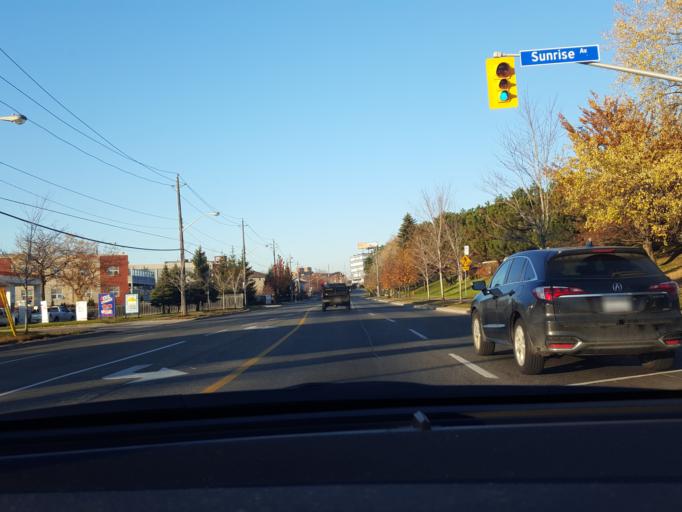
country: CA
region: Ontario
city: Scarborough
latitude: 43.7190
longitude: -79.3044
